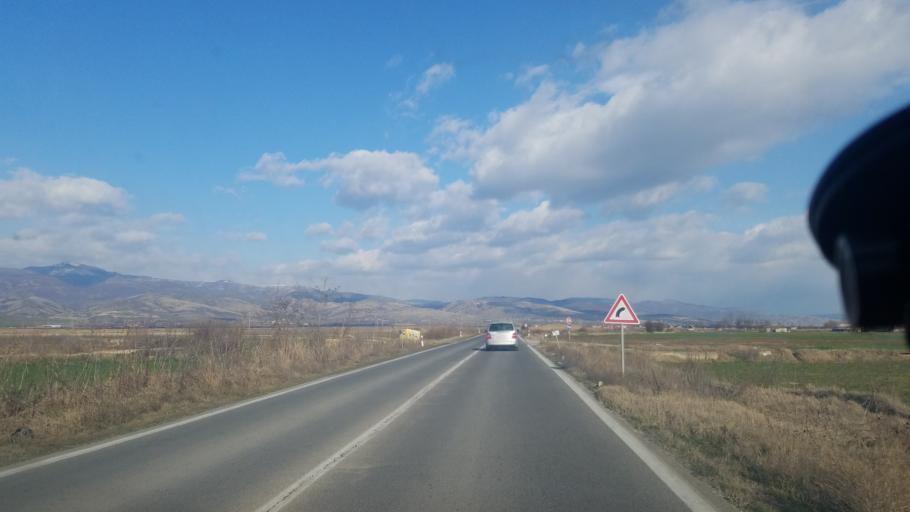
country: MK
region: Cesinovo-Oblesevo
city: Cesinovo
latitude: 41.8699
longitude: 22.3100
